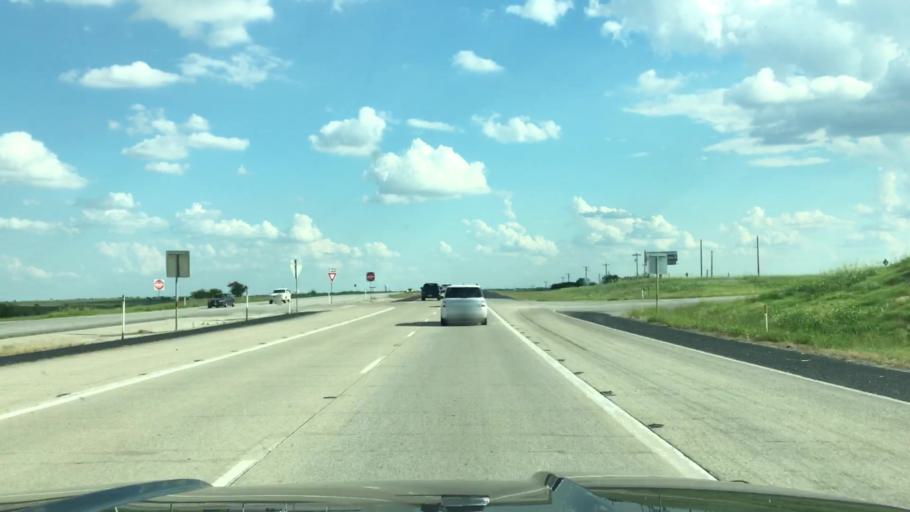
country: US
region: Texas
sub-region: Wise County
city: Newark
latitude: 33.0121
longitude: -97.4388
